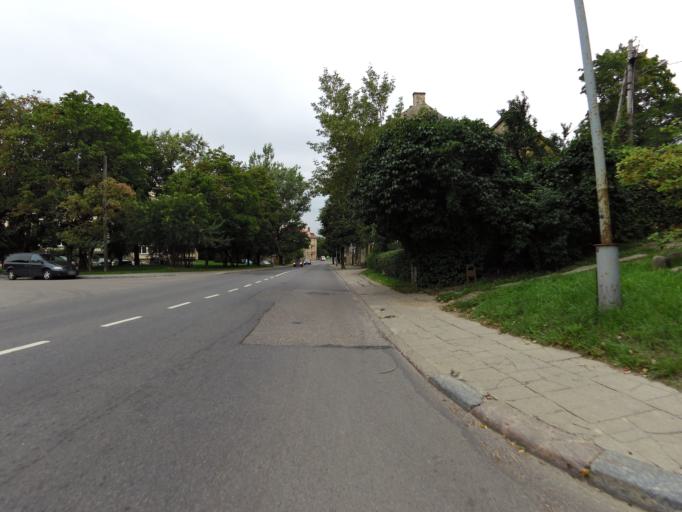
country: LT
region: Vilnius County
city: Rasos
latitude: 54.6697
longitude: 25.2945
